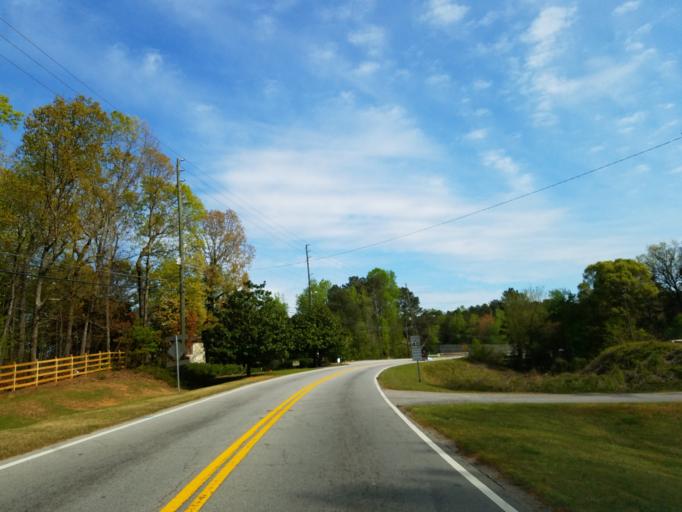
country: US
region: Georgia
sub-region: Douglas County
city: Lithia Springs
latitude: 33.7732
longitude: -84.6380
